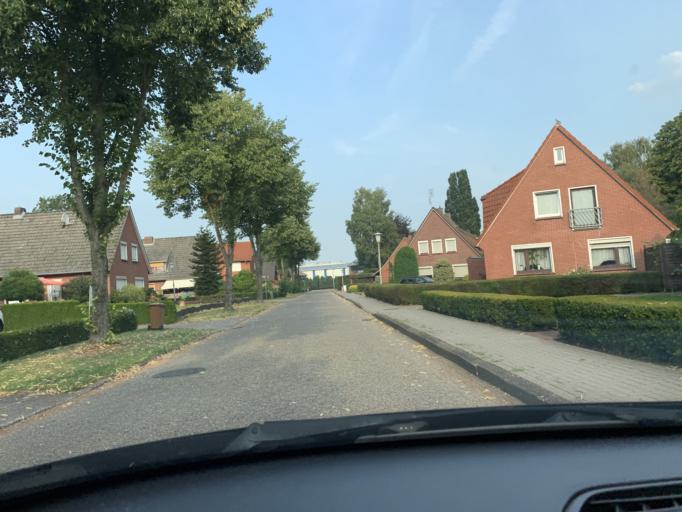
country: DE
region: Lower Saxony
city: Apen
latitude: 53.2234
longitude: 7.8142
